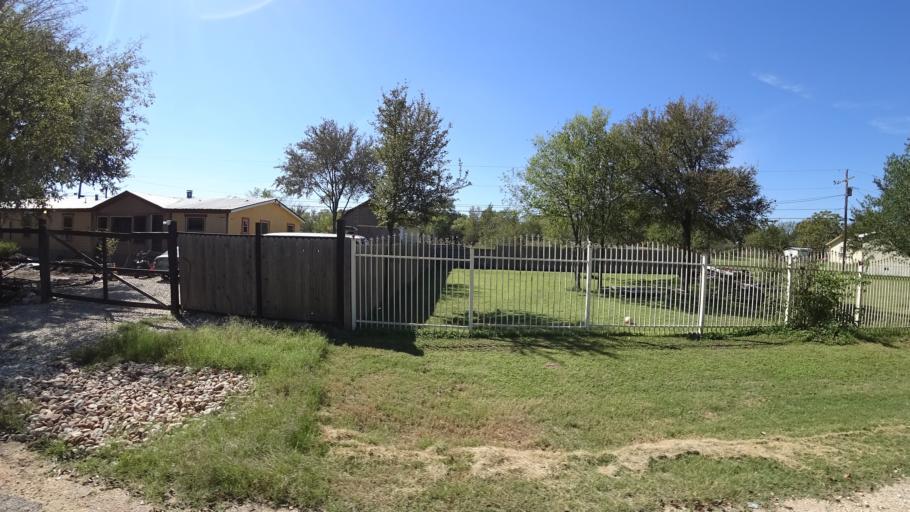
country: US
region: Texas
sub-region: Travis County
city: Hornsby Bend
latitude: 30.2700
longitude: -97.6181
